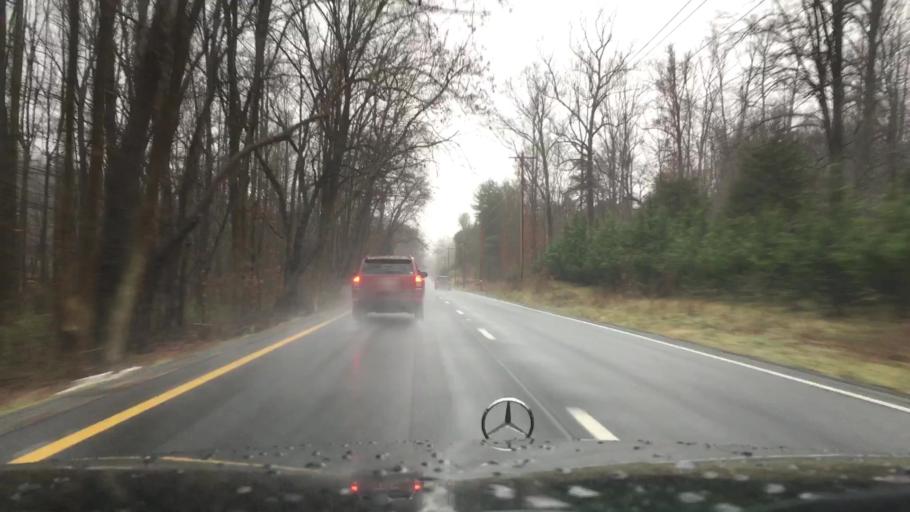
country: US
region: Virginia
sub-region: Albemarle County
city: Crozet
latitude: 37.9397
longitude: -78.6693
